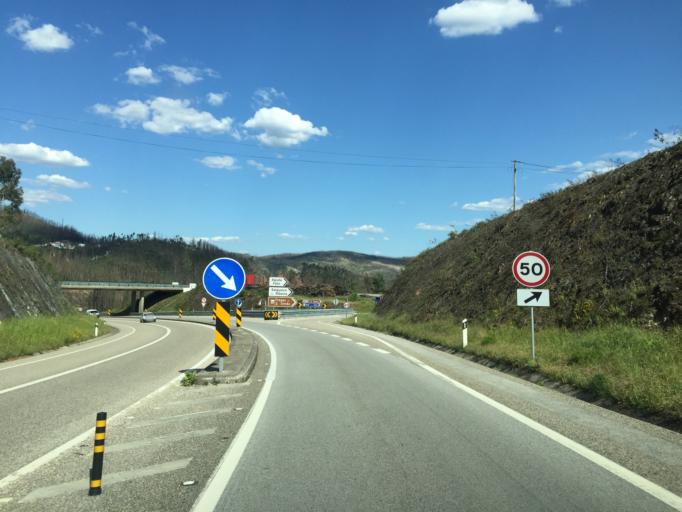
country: PT
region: Leiria
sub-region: Figueiro Dos Vinhos
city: Figueiro dos Vinhos
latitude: 39.9266
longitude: -8.3308
